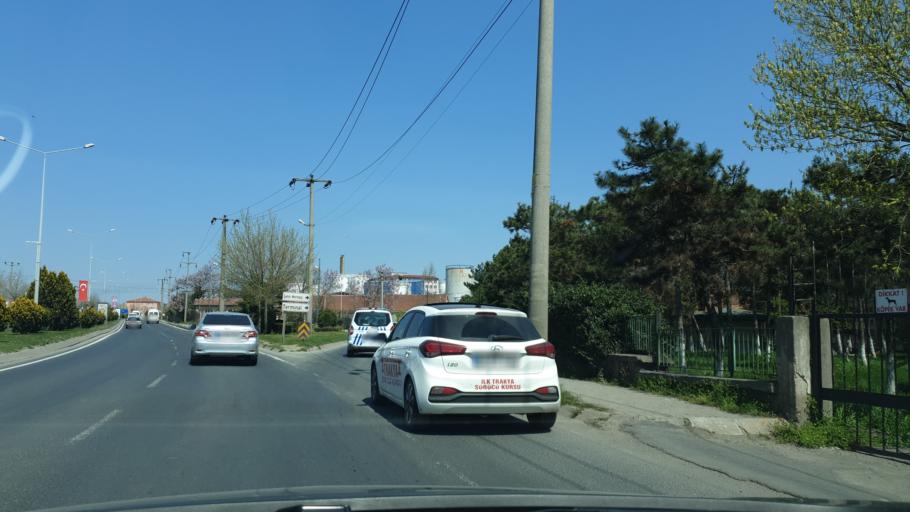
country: TR
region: Tekirdag
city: Corlu
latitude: 41.1599
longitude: 27.7861
